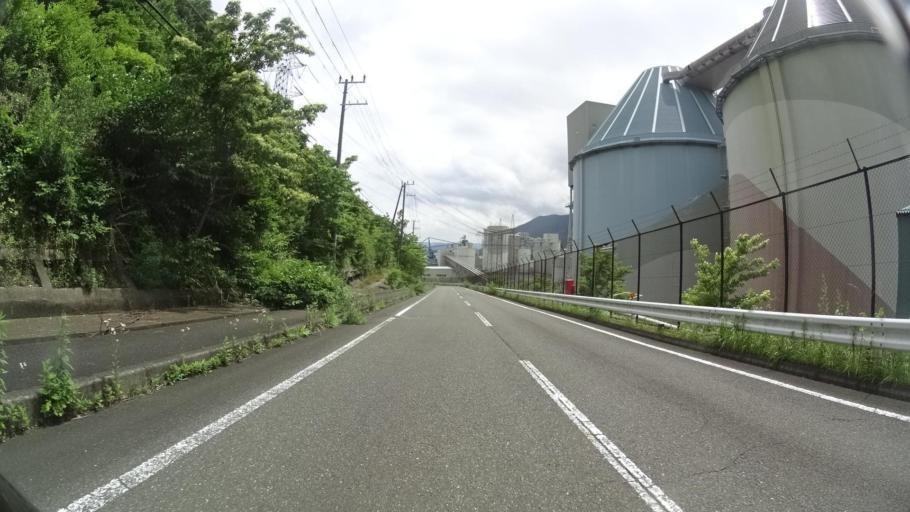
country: JP
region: Kyoto
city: Maizuru
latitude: 35.5262
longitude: 135.3446
